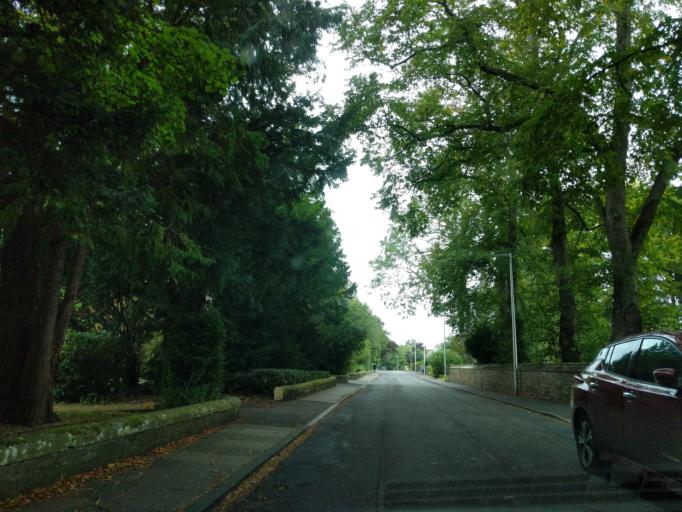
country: GB
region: Scotland
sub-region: The Scottish Borders
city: Melrose
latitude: 55.5992
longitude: -2.7314
